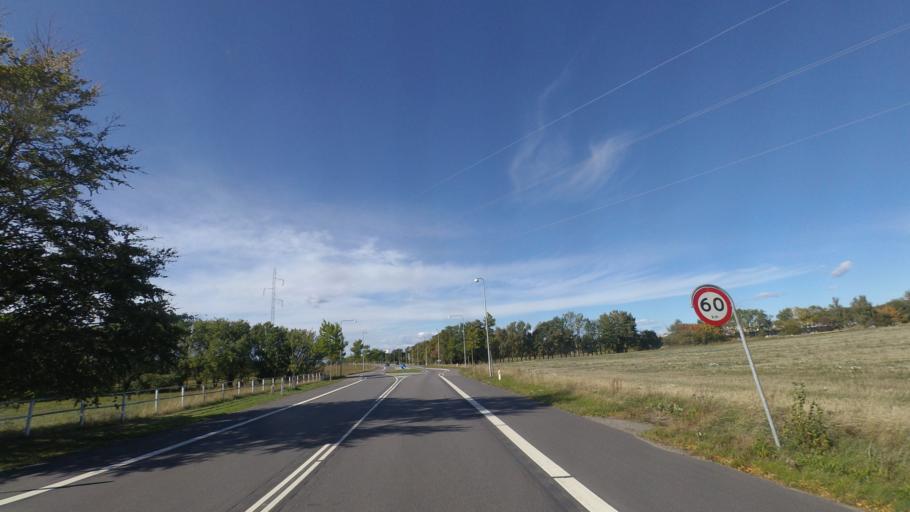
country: DK
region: Capital Region
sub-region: Bornholm Kommune
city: Ronne
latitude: 55.0896
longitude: 14.7387
